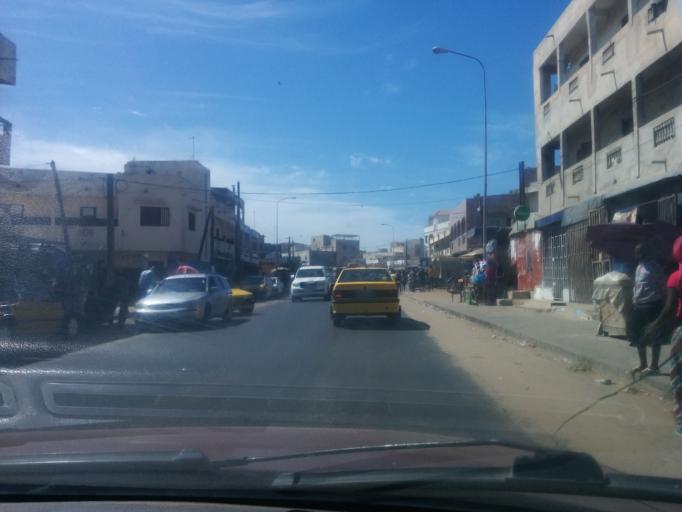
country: SN
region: Dakar
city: Pikine
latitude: 14.7792
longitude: -17.3915
